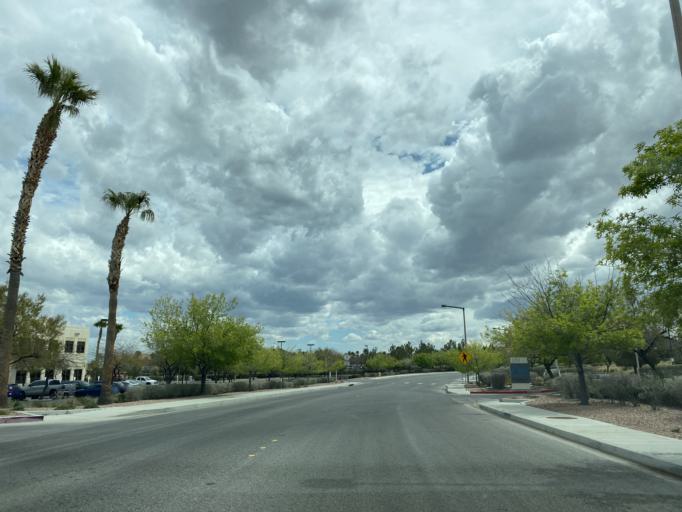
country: US
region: Nevada
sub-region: Clark County
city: Summerlin South
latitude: 36.1880
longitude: -115.3115
